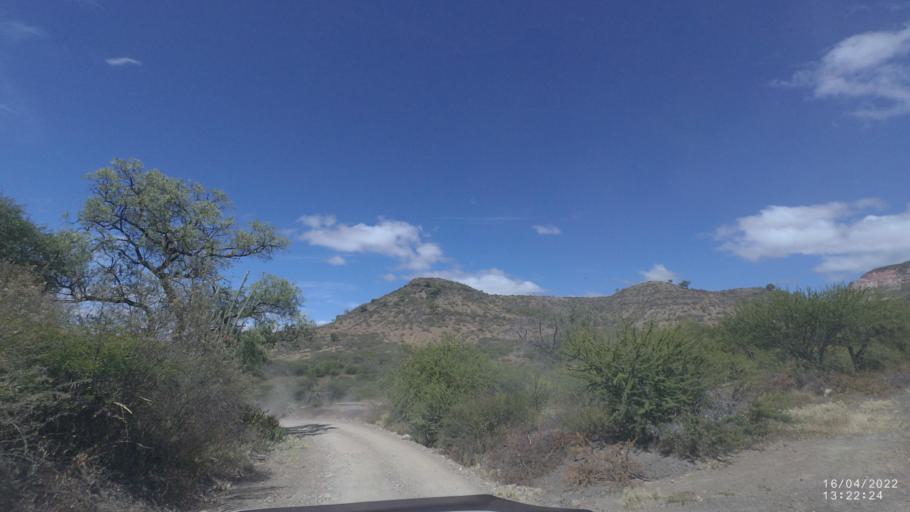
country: BO
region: Cochabamba
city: Mizque
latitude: -17.9929
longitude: -65.6062
